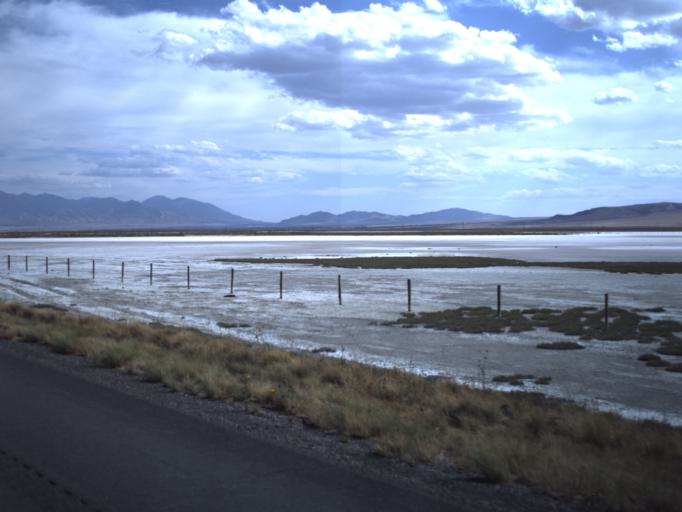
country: US
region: Utah
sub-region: Tooele County
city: Grantsville
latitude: 40.7181
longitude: -112.5507
